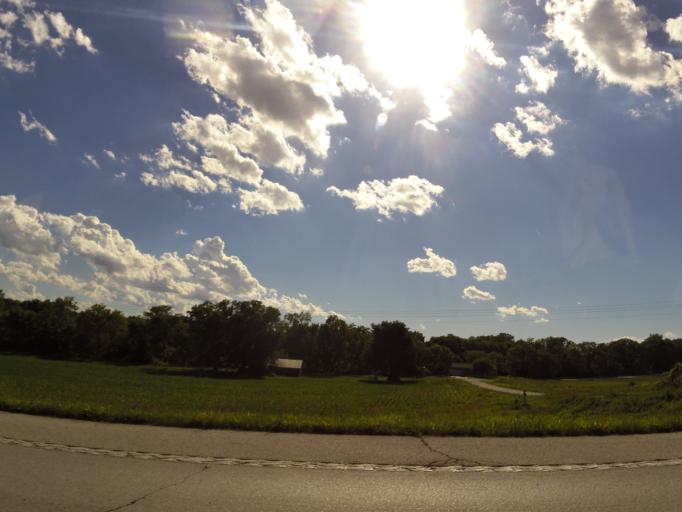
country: US
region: Missouri
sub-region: Marion County
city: Palmyra
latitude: 39.9028
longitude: -91.5256
